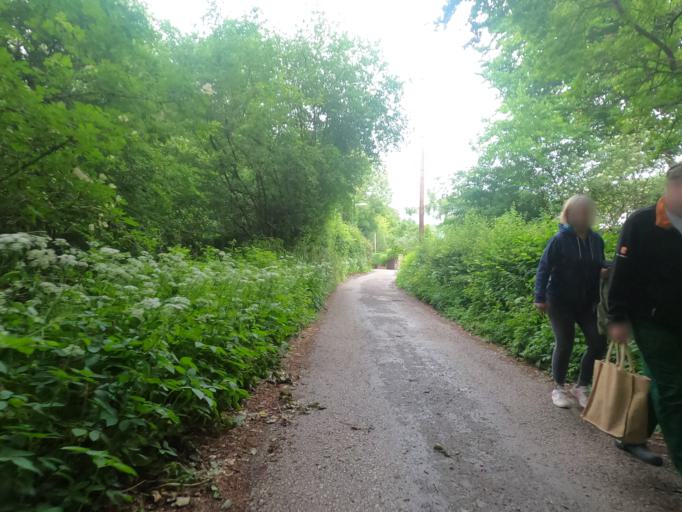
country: GB
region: England
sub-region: Cheshire West and Chester
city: Cuddington
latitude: 53.2370
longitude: -2.6125
